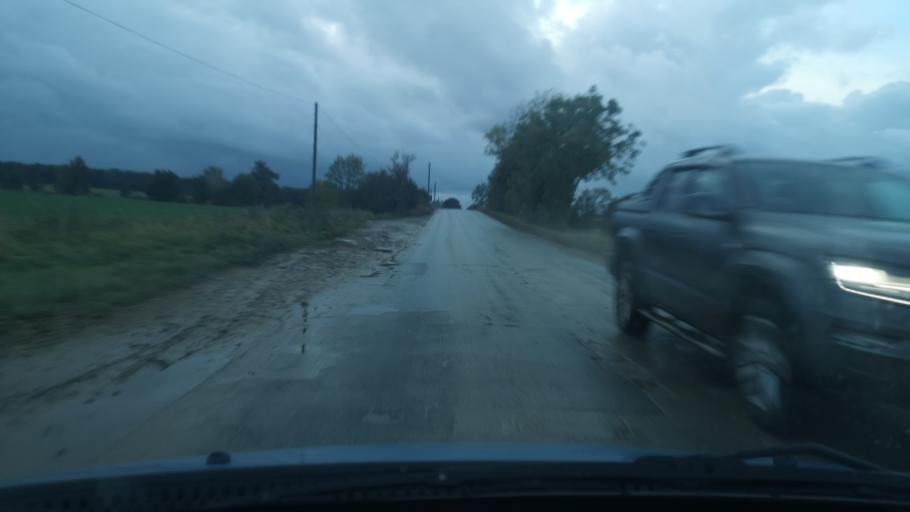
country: GB
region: England
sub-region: City and Borough of Wakefield
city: Darrington
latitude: 53.6466
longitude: -1.2536
